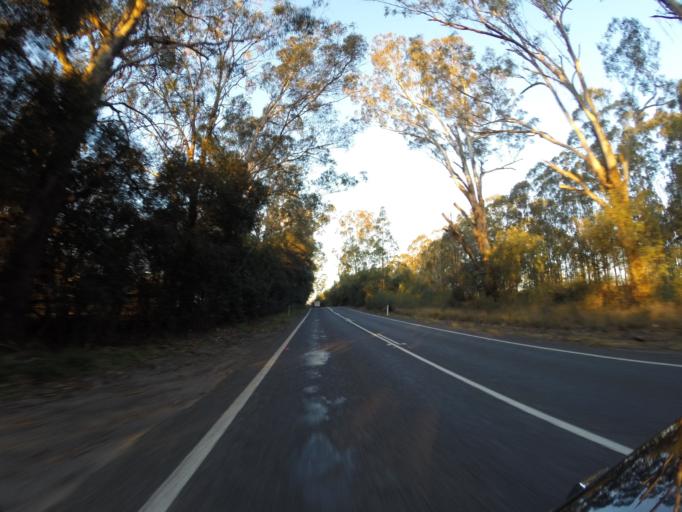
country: AU
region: New South Wales
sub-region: Camden
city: Cobbitty
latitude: -34.0156
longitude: 150.7039
